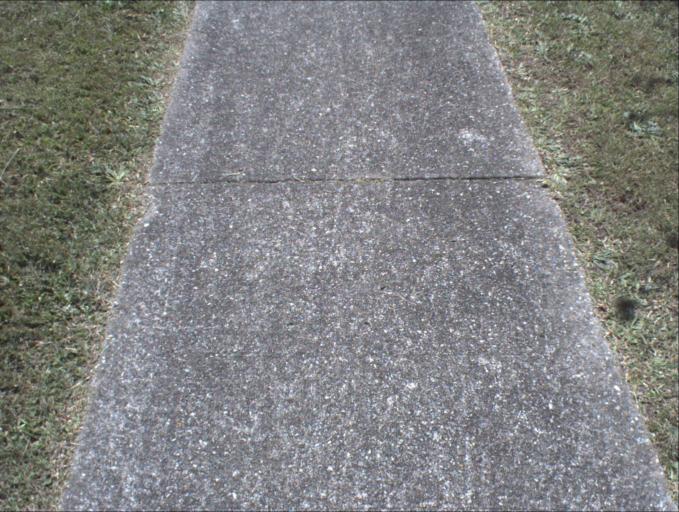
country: AU
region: Queensland
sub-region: Logan
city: Springwood
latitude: -27.6025
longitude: 153.1364
